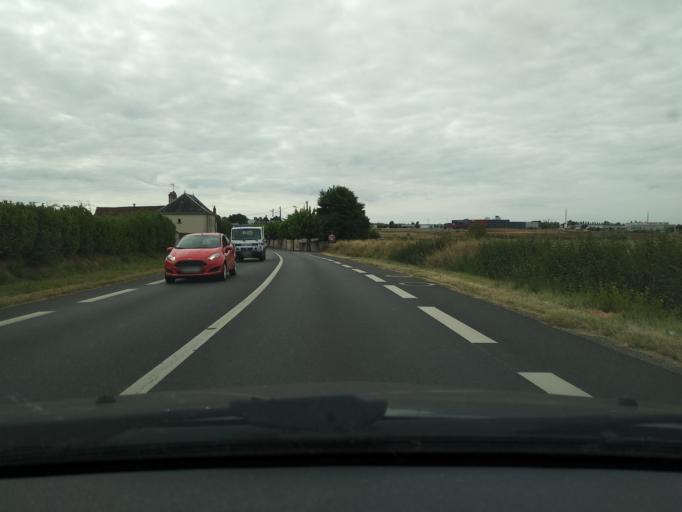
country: FR
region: Centre
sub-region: Departement d'Indre-et-Loire
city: Chanceaux-sur-Choisille
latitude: 47.4463
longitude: 0.6986
